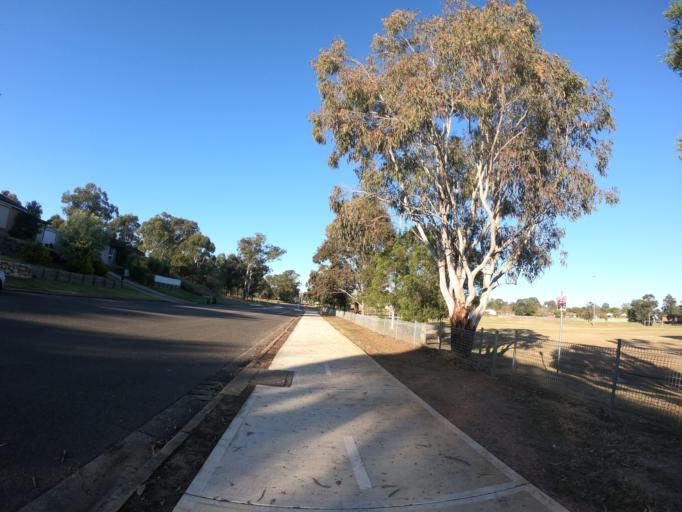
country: AU
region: New South Wales
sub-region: Hawkesbury
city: South Windsor
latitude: -33.6293
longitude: 150.8096
